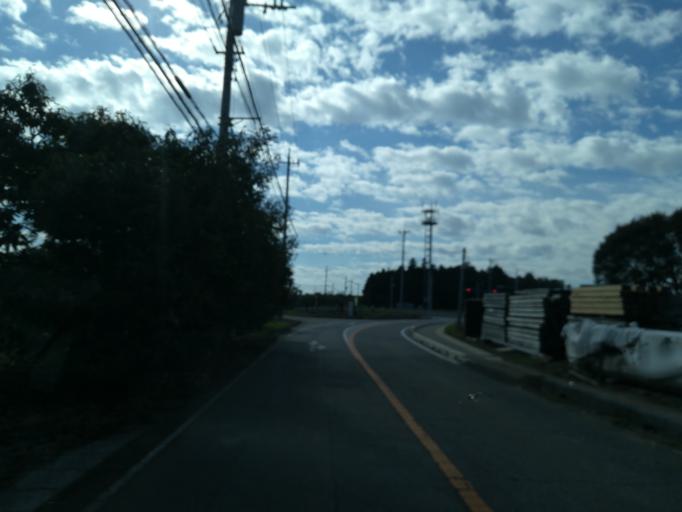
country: JP
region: Ibaraki
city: Naka
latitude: 36.0614
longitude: 140.0870
